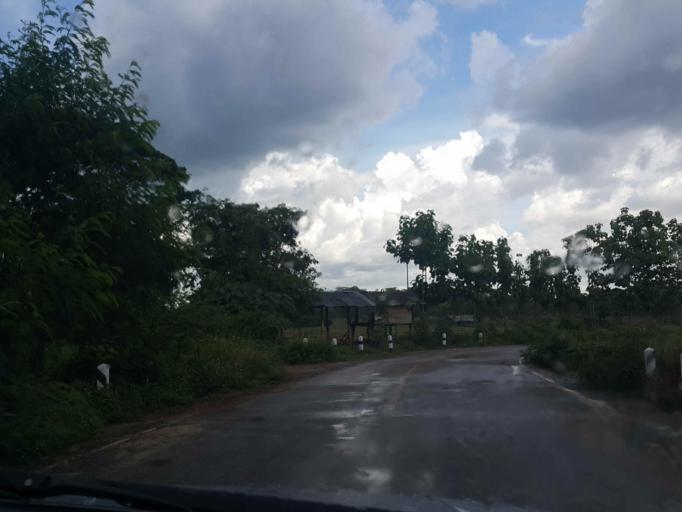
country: TH
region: Phayao
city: Dok Kham Tai
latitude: 19.0397
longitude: 99.9803
